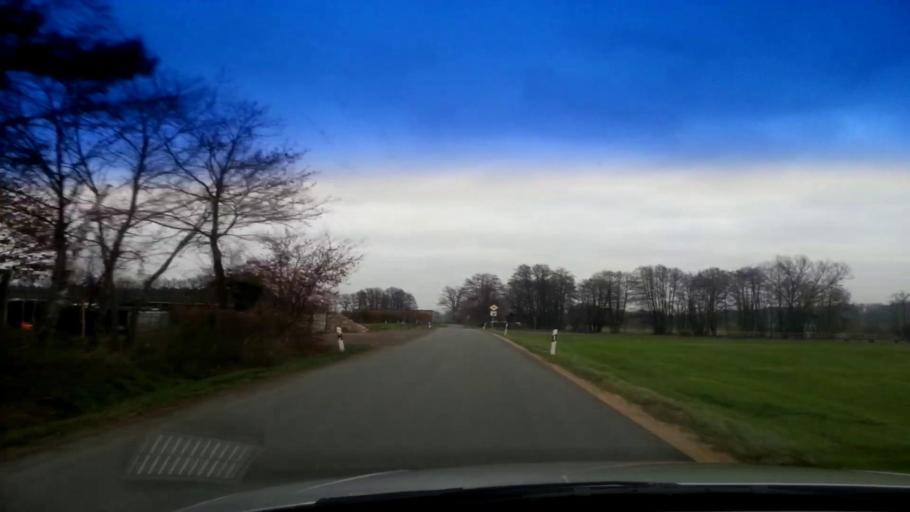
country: DE
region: Bavaria
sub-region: Upper Franconia
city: Walsdorf
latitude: 49.8221
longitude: 10.8056
